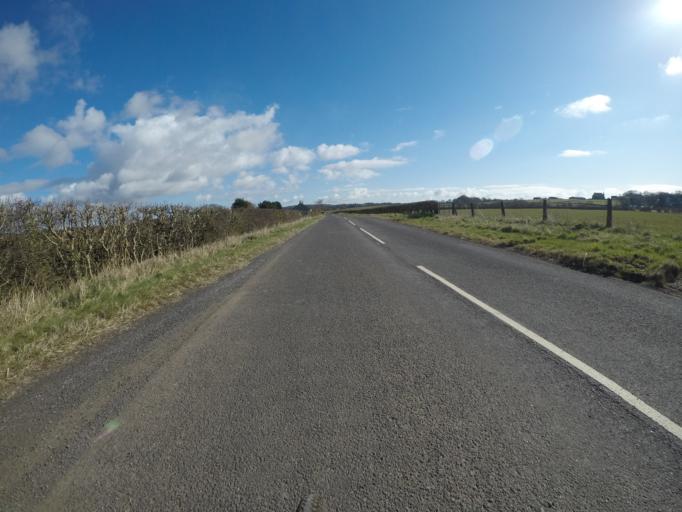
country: GB
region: Scotland
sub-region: North Ayrshire
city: Irvine
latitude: 55.6532
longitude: -4.6544
